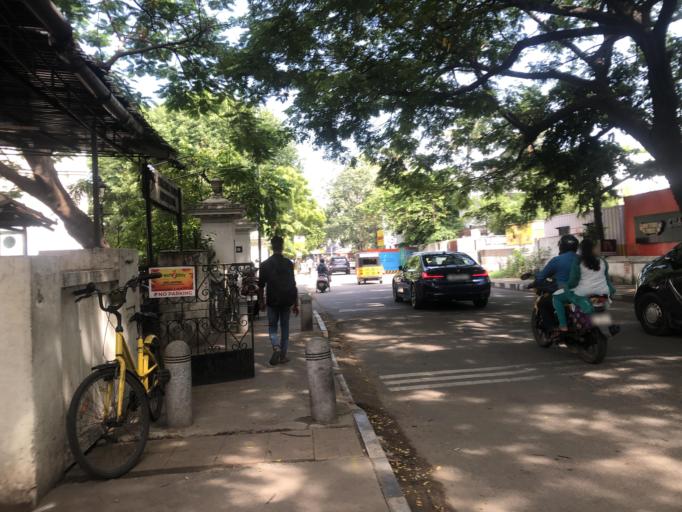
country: IN
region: Tamil Nadu
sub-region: Chennai
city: Gandhi Nagar
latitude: 13.0382
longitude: 80.2598
